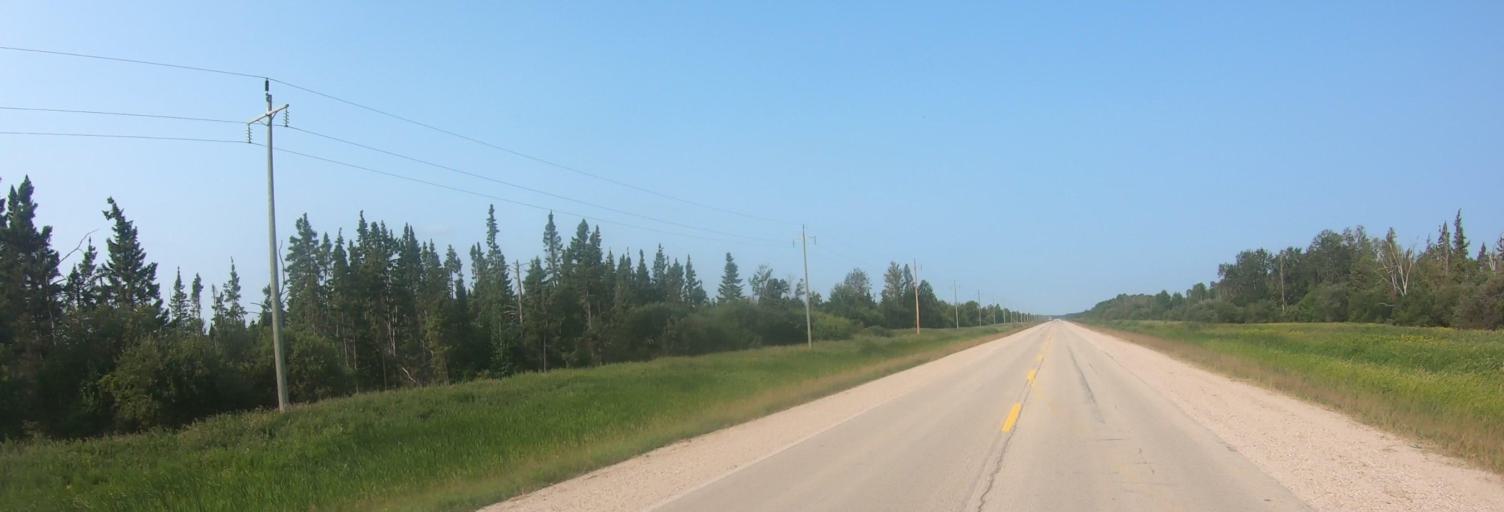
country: US
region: Minnesota
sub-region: Roseau County
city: Roseau
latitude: 49.0234
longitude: -95.6742
